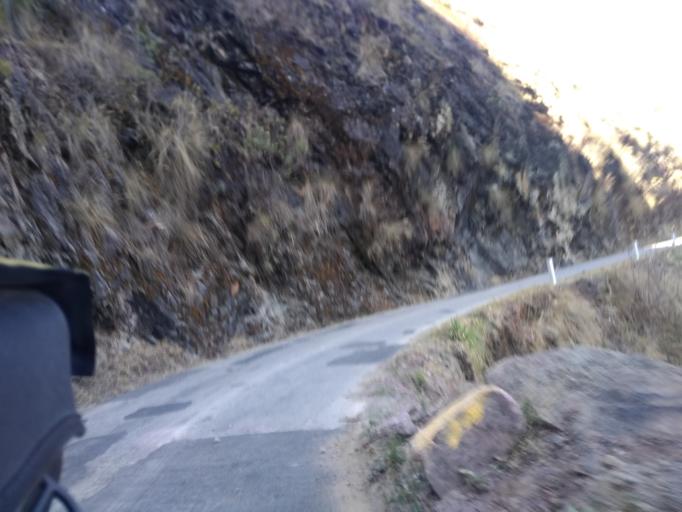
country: PE
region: Amazonas
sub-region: Provincia de Chachapoyas
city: Balsas
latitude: -6.7940
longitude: -77.9422
